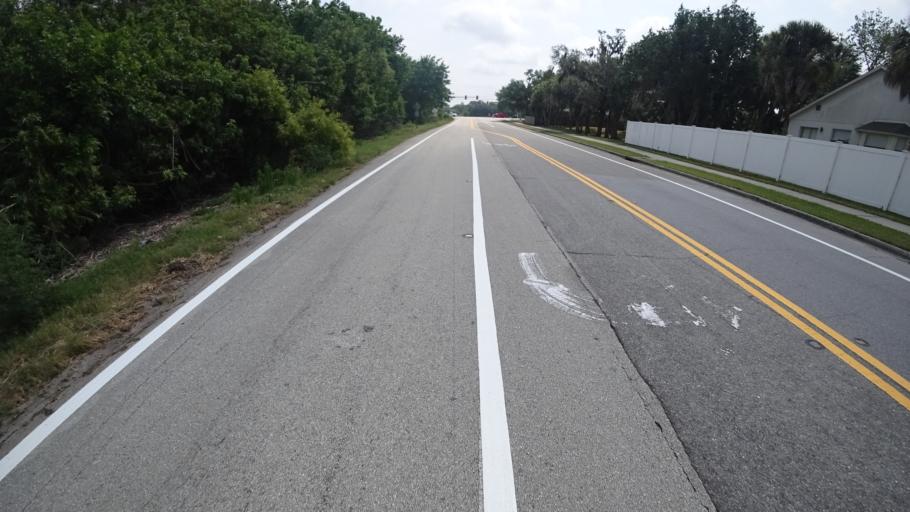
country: US
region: Florida
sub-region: Sarasota County
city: North Sarasota
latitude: 27.4181
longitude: -82.5066
